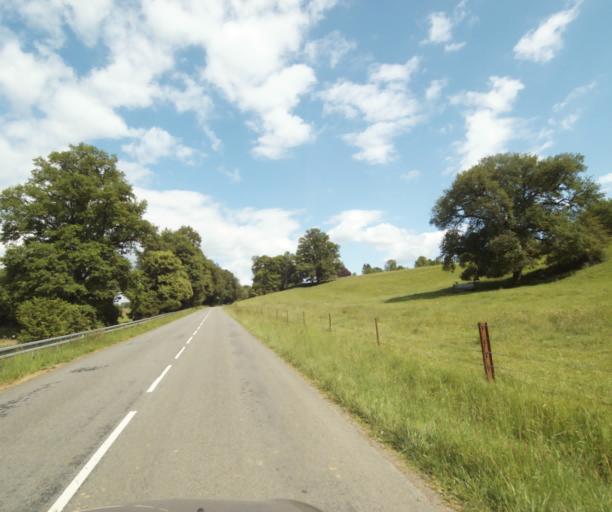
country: FR
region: Champagne-Ardenne
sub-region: Departement des Ardennes
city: Saint-Laurent
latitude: 49.7638
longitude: 4.7613
